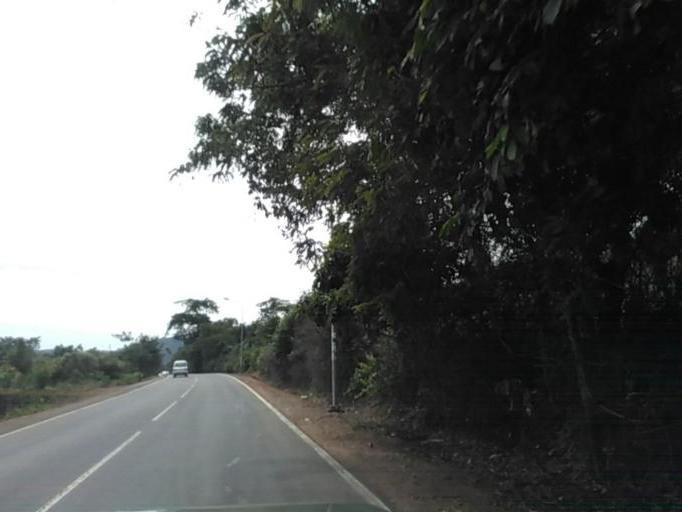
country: GH
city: Akropong
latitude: 6.2669
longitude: 0.0709
